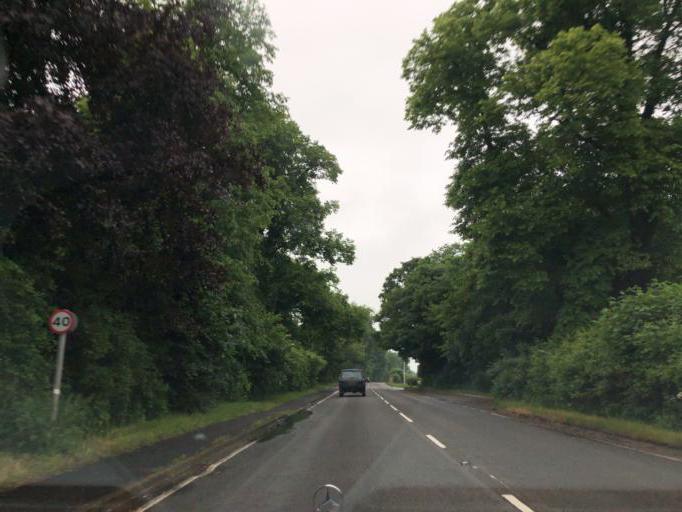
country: GB
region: England
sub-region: Warwickshire
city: Wroxall
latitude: 52.3050
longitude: -1.6570
